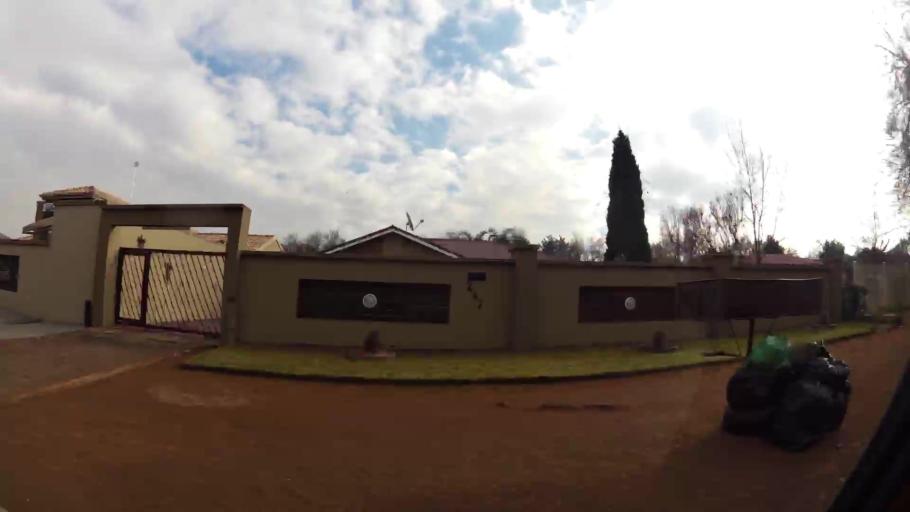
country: ZA
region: Gauteng
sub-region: Sedibeng District Municipality
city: Vanderbijlpark
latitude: -26.7047
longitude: 27.8260
